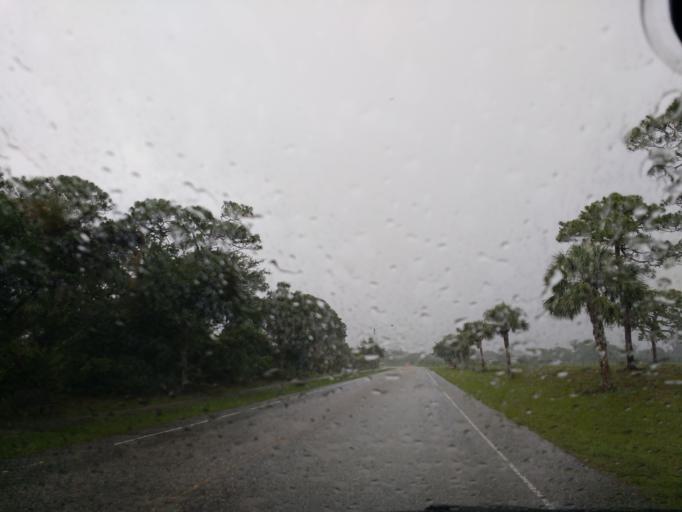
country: US
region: Florida
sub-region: Sarasota County
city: Venice
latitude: 27.0755
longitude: -82.4494
